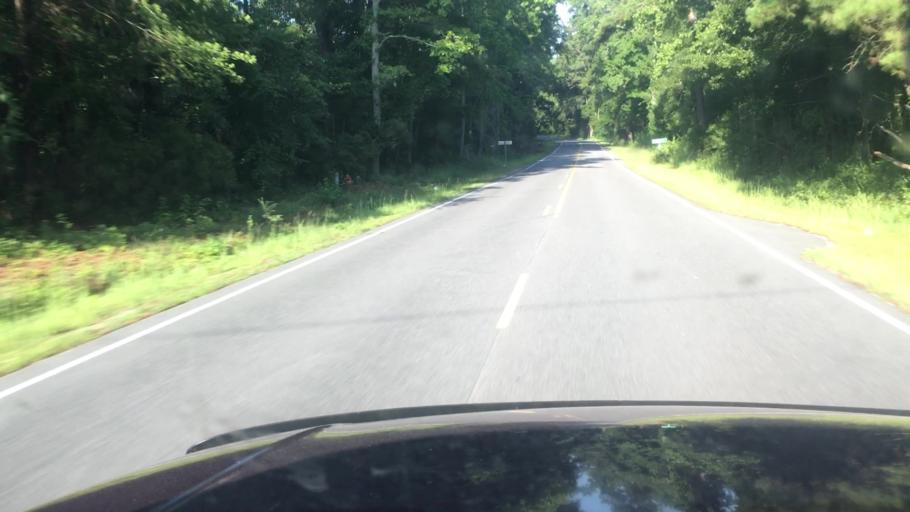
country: US
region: North Carolina
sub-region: Robeson County
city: Saint Pauls
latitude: 34.8337
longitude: -78.9000
